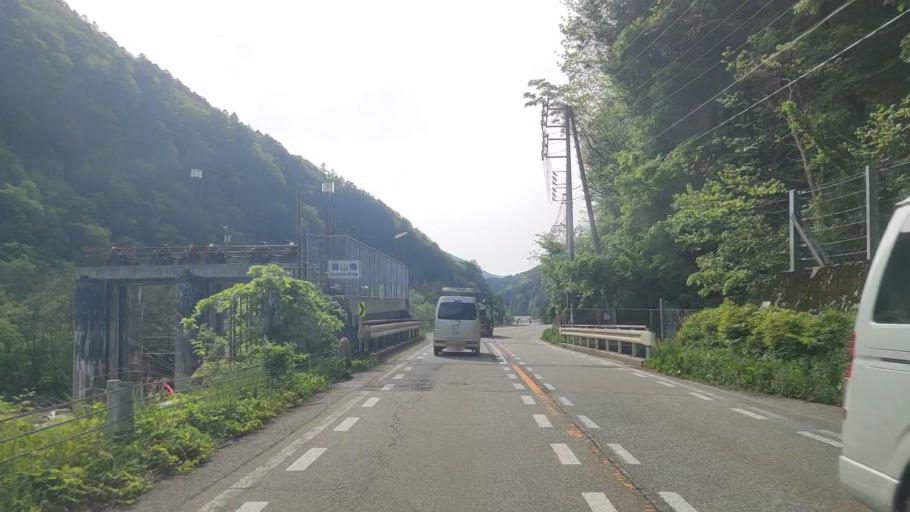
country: JP
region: Gifu
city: Takayama
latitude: 36.2655
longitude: 137.4277
